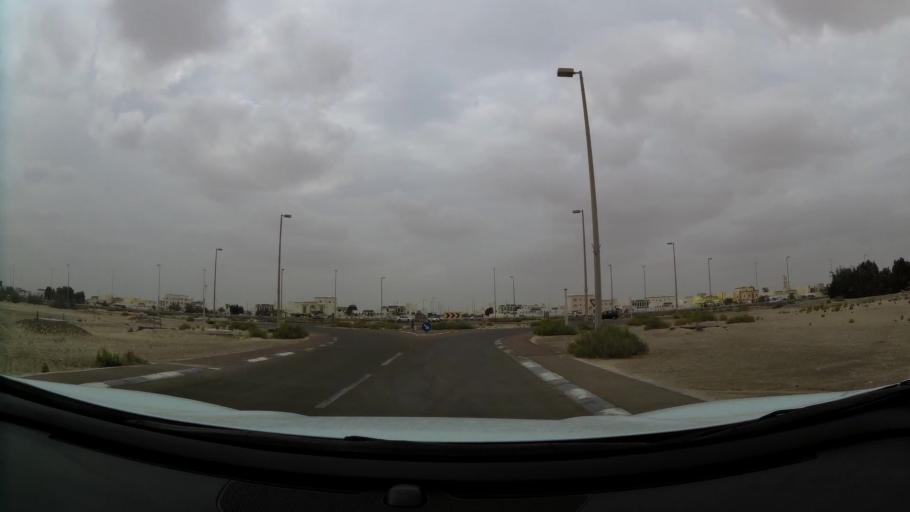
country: AE
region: Abu Dhabi
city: Abu Dhabi
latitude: 24.3433
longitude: 54.6493
